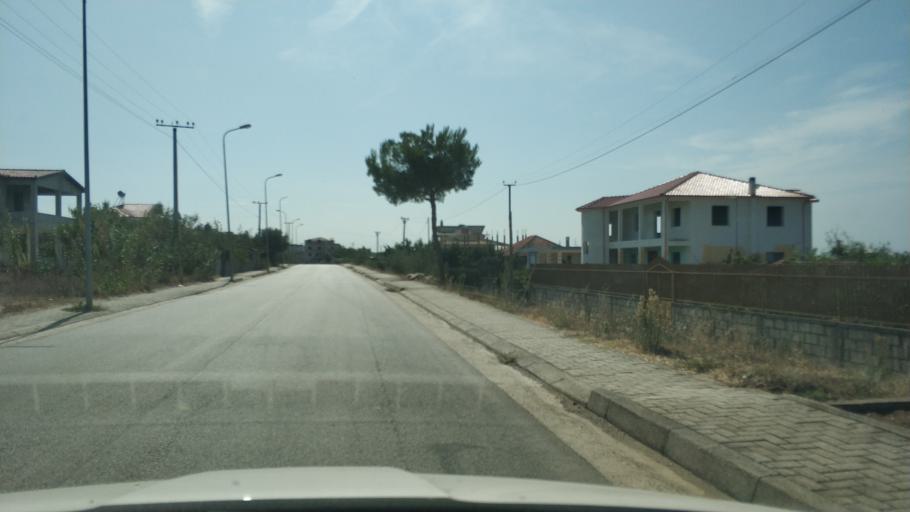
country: AL
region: Fier
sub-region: Rrethi i Lushnjes
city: Divjake
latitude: 40.9801
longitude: 19.5351
